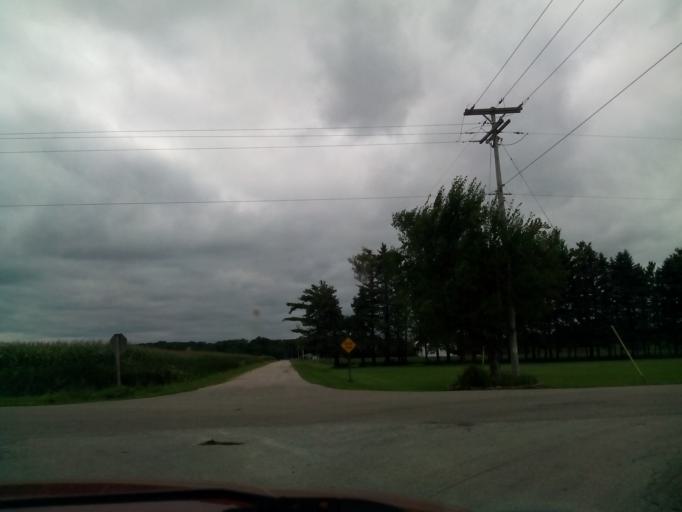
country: US
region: Wisconsin
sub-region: Outagamie County
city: Black Creek
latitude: 44.5239
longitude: -88.4700
